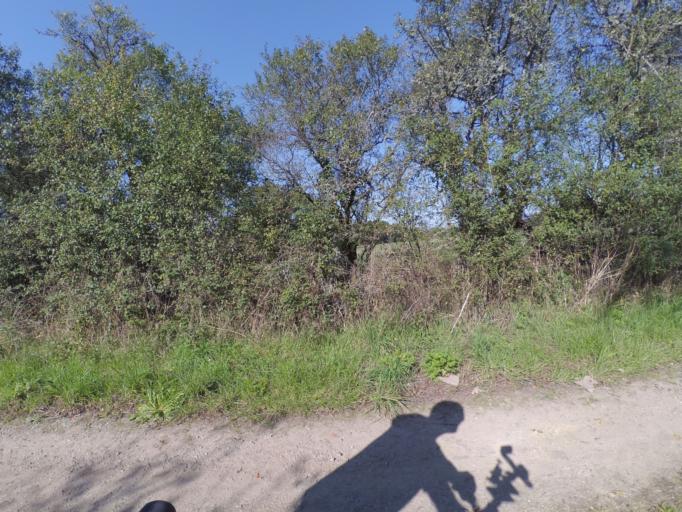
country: FR
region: Pays de la Loire
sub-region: Departement de la Loire-Atlantique
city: Chemere
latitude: 47.1114
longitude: -1.9026
